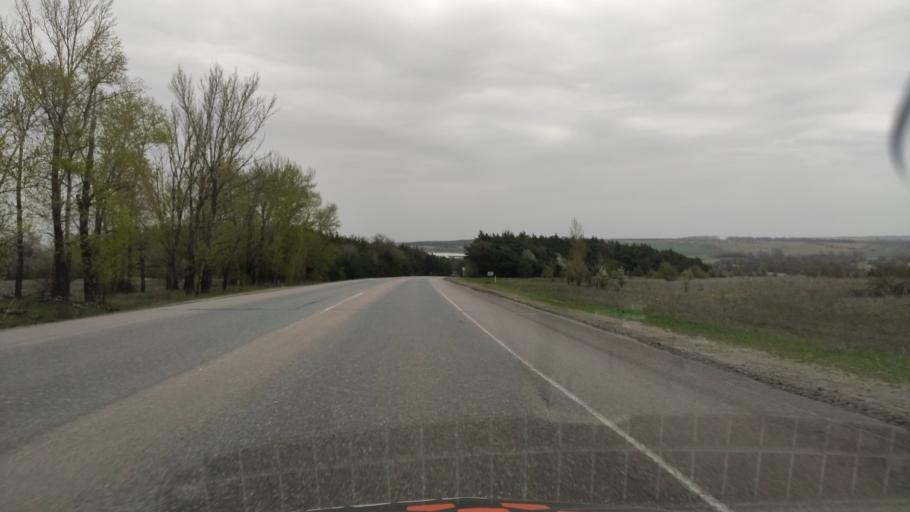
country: RU
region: Kursk
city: Gorshechnoye
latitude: 51.4627
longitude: 37.9258
